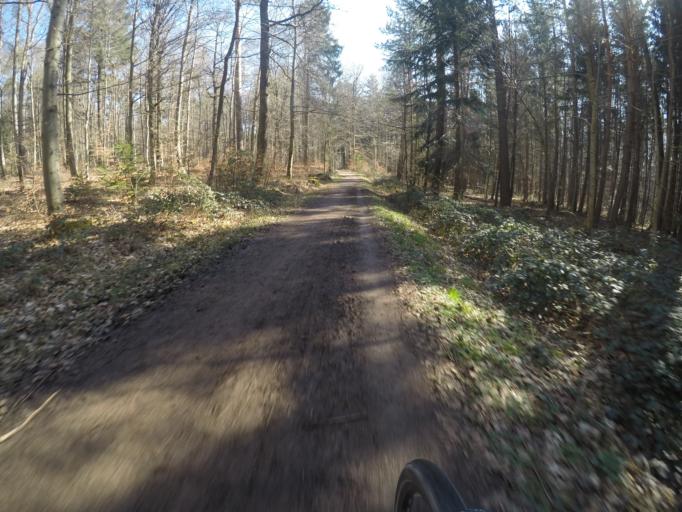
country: DE
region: Baden-Wuerttemberg
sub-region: Regierungsbezirk Stuttgart
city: Stuttgart
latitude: 48.7606
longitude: 9.1218
